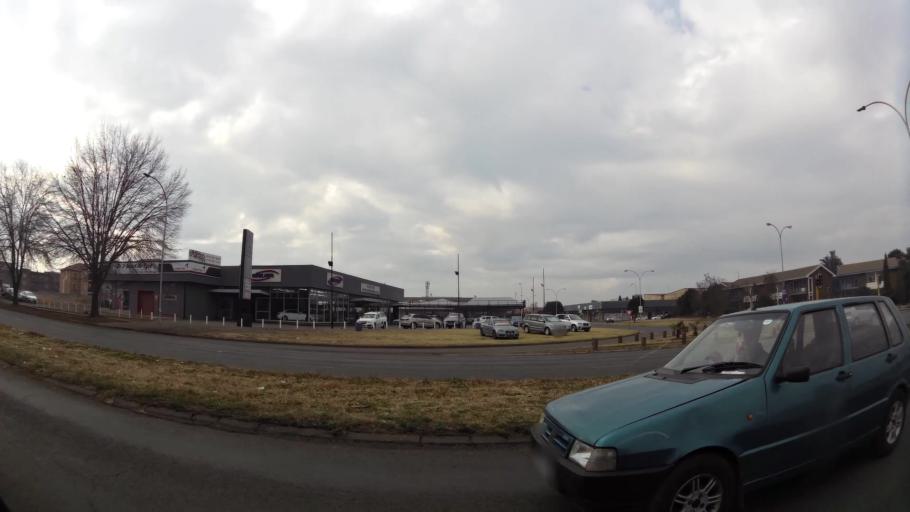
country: ZA
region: Gauteng
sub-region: Sedibeng District Municipality
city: Vanderbijlpark
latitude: -26.6976
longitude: 27.8322
